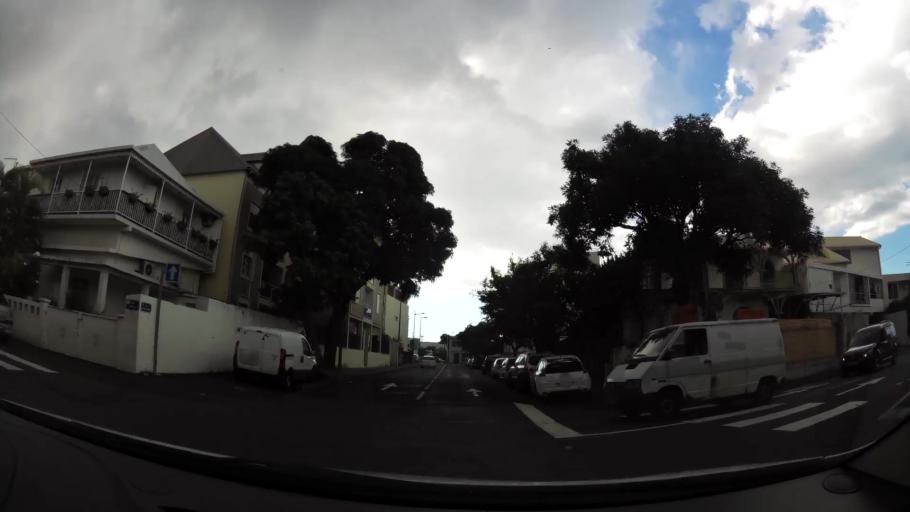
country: RE
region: Reunion
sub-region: Reunion
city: Saint-Denis
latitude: -20.8865
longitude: 55.4550
